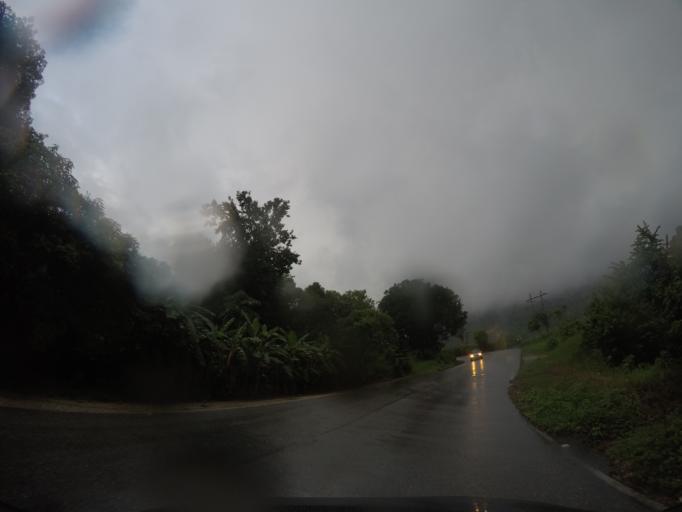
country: MX
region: Oaxaca
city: San Gabriel Mixtepec
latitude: 16.0749
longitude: -97.0834
